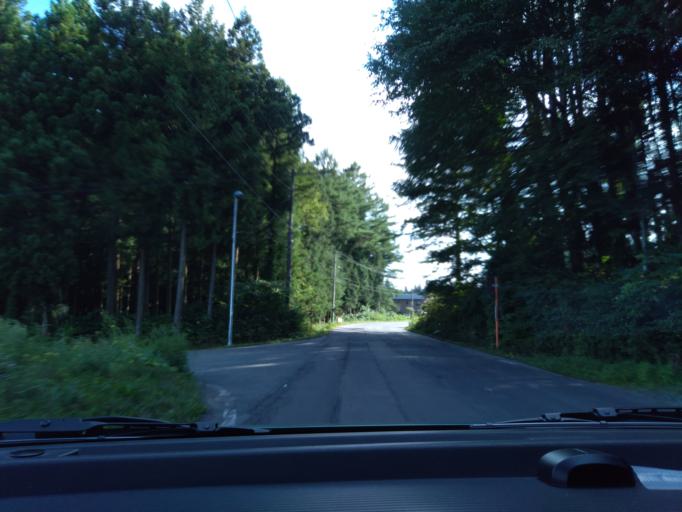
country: JP
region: Iwate
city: Morioka-shi
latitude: 39.5847
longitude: 141.0881
